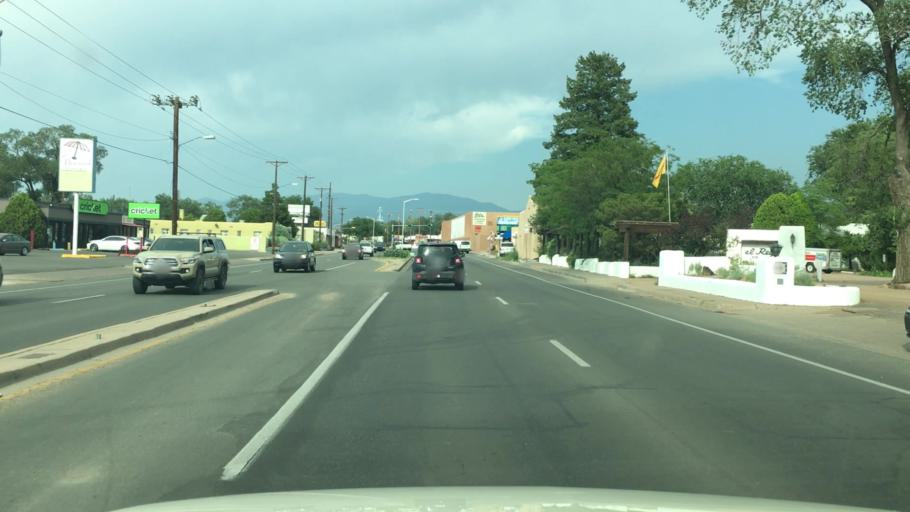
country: US
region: New Mexico
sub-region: Santa Fe County
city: Santa Fe
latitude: 35.6644
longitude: -105.9736
